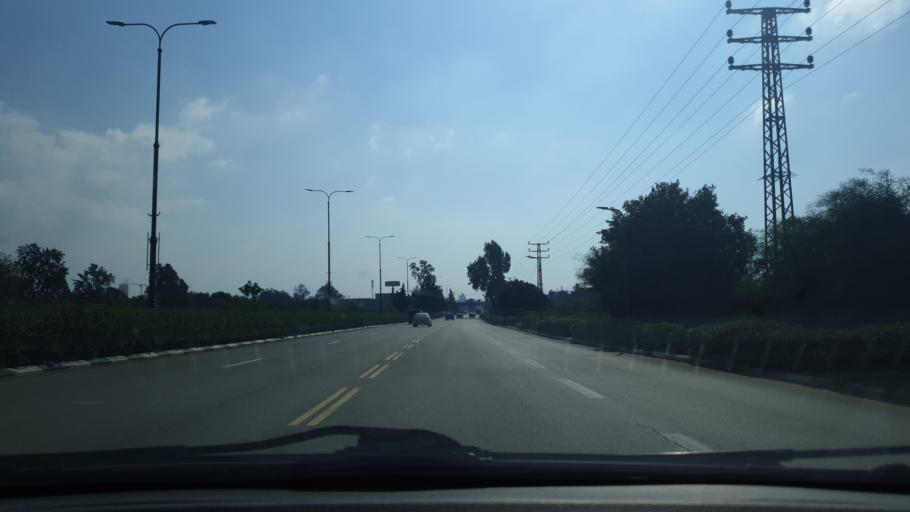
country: IL
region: Central District
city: Bet Dagan
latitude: 31.9892
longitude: 34.8119
